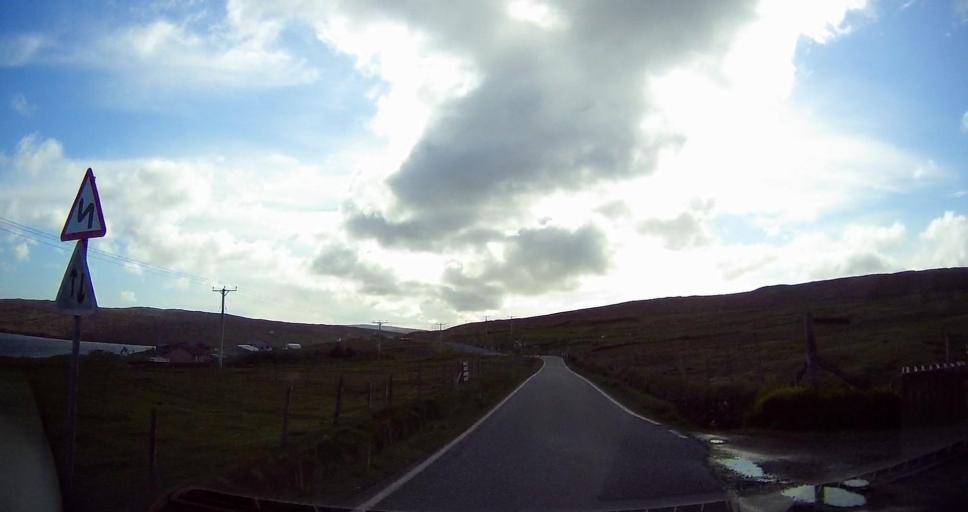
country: GB
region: Scotland
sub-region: Shetland Islands
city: Shetland
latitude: 60.3559
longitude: -1.1635
